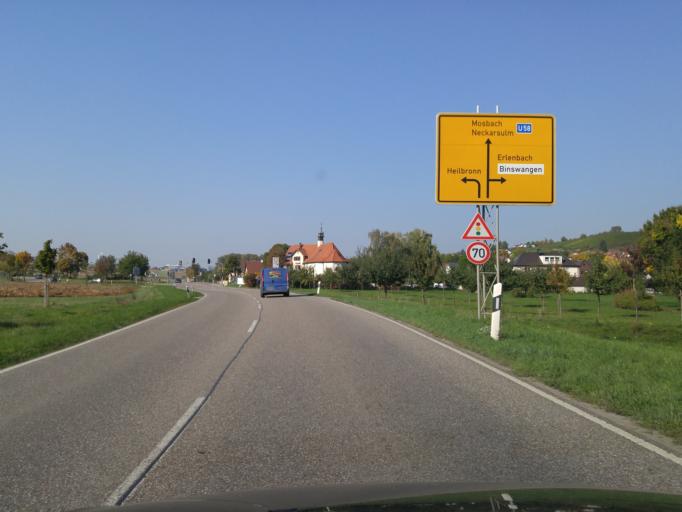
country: DE
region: Baden-Wuerttemberg
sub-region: Regierungsbezirk Stuttgart
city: Erlenbach
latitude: 49.1700
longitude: 9.2612
